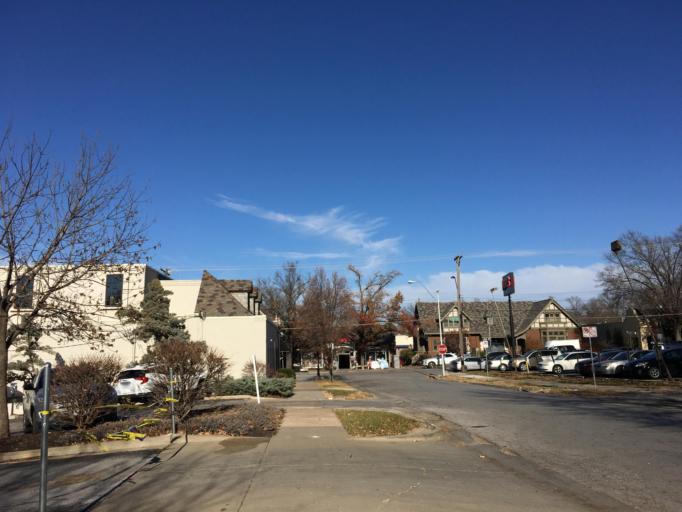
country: US
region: Kansas
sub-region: Johnson County
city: Mission Hills
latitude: 39.0133
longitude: -94.5896
